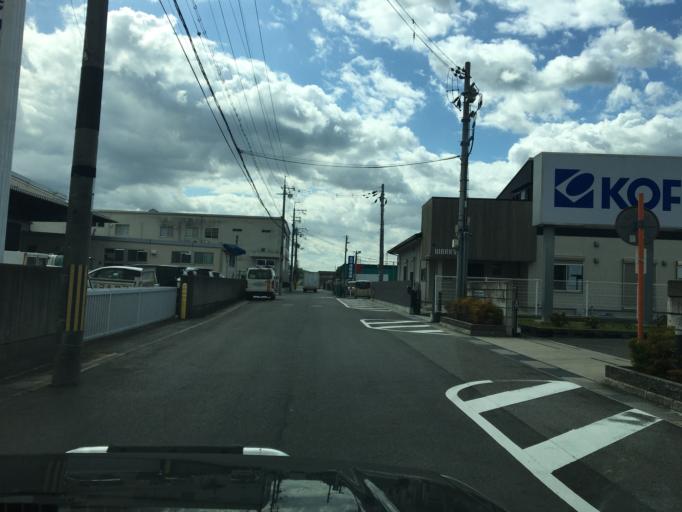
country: JP
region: Kyoto
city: Tanabe
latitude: 34.8172
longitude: 135.7908
